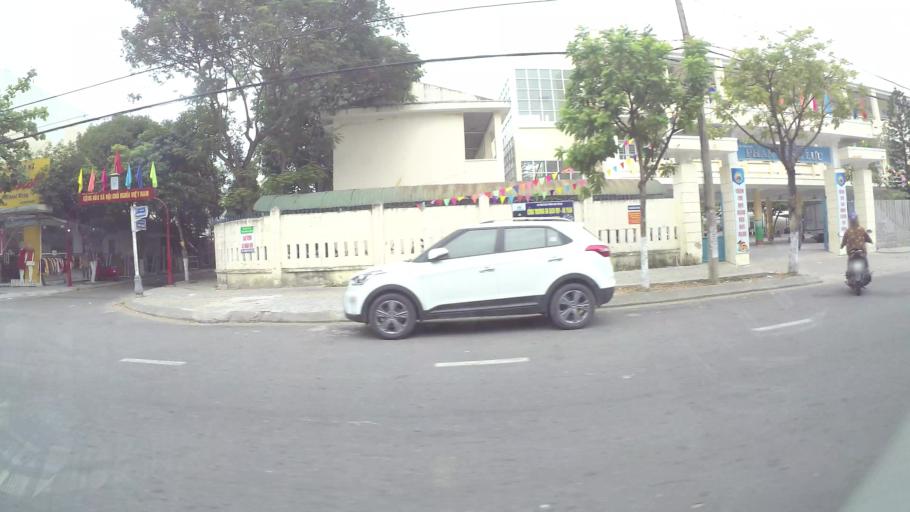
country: VN
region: Da Nang
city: Cam Le
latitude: 16.0366
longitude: 108.2177
